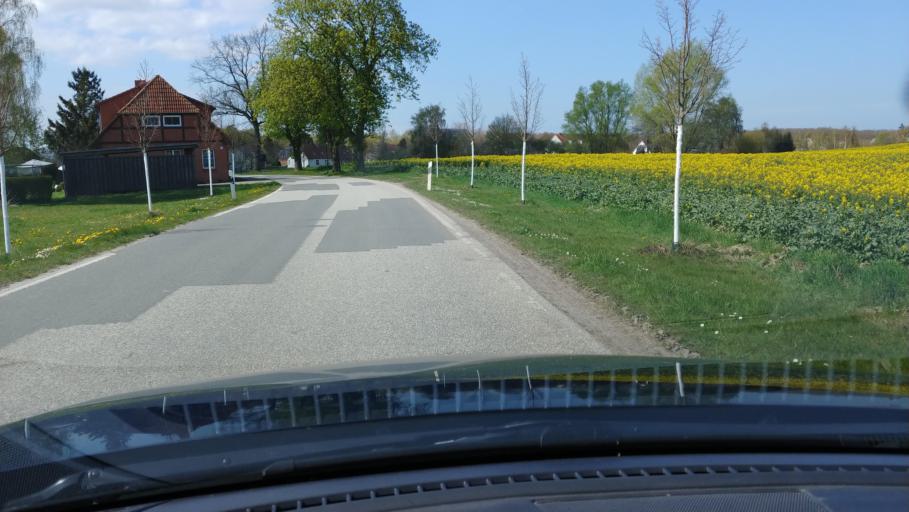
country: DE
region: Mecklenburg-Vorpommern
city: Muhlen Eichsen
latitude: 53.7780
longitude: 11.2676
